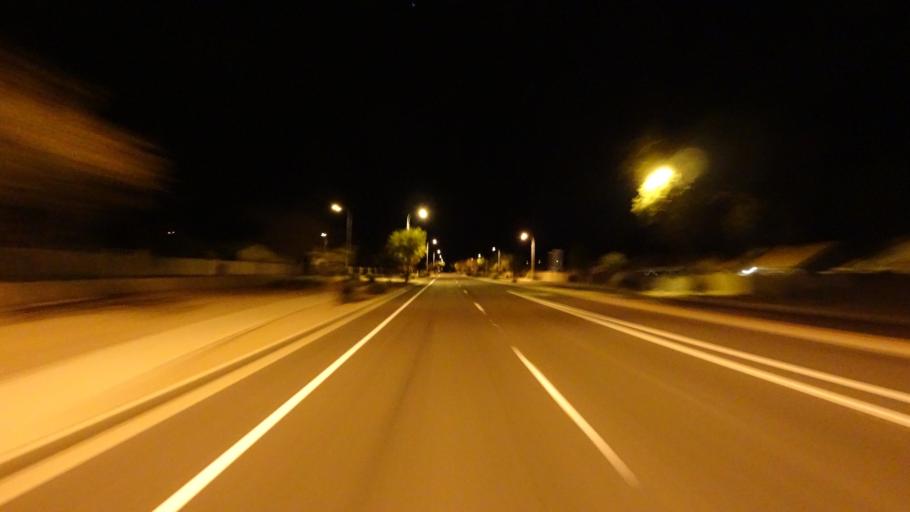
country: US
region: Arizona
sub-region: Maricopa County
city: Sun Lakes
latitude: 33.2081
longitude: -111.8064
